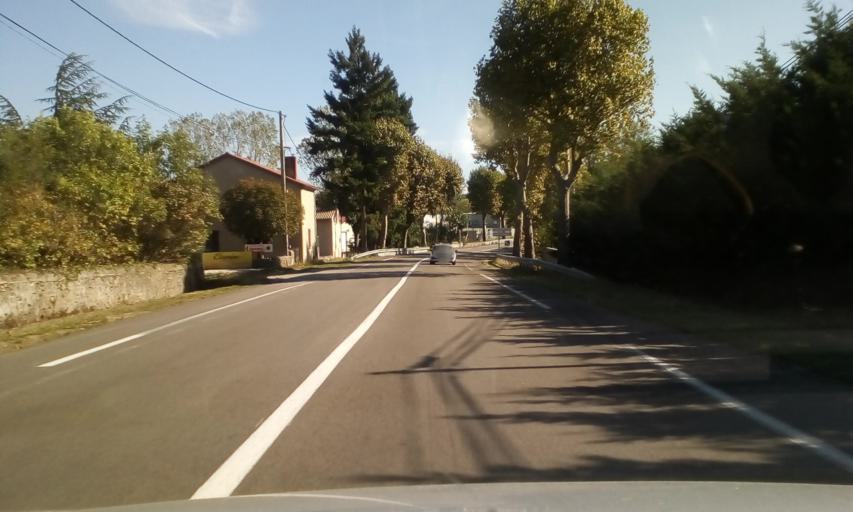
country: FR
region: Rhone-Alpes
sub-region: Departement de l'Ardeche
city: Annonay
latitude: 45.2546
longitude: 4.6744
